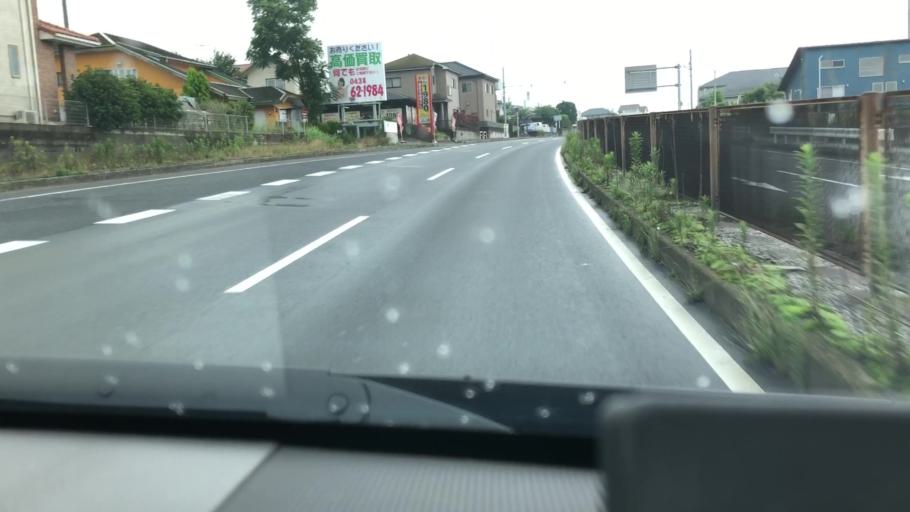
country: JP
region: Chiba
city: Kisarazu
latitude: 35.4340
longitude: 139.9697
